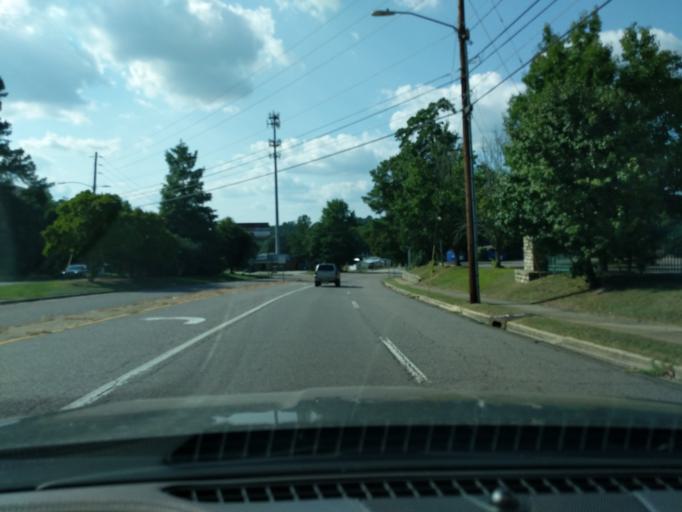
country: US
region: Georgia
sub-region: Richmond County
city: Augusta
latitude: 33.4899
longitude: -82.0072
